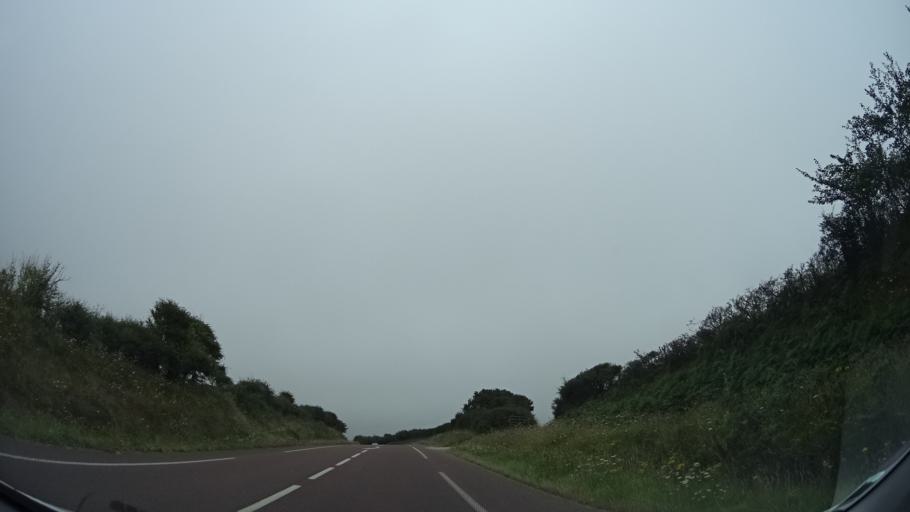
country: FR
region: Lower Normandy
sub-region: Departement de la Manche
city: Flamanville
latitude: 49.5489
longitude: -1.8540
